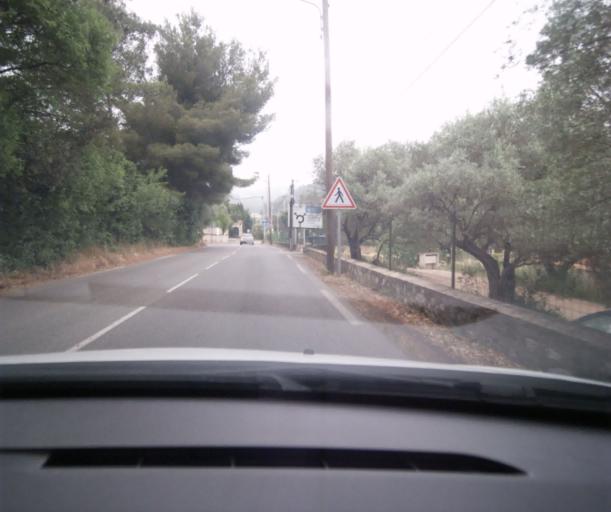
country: FR
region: Provence-Alpes-Cote d'Azur
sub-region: Departement du Var
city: La Valette-du-Var
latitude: 43.1463
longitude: 5.9785
